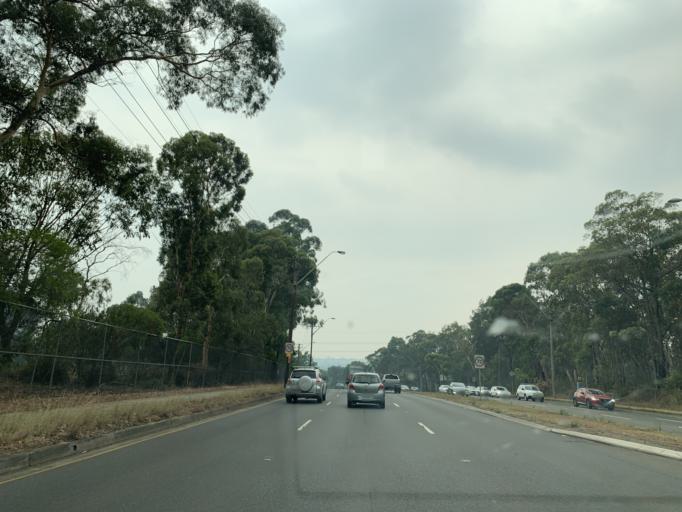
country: AU
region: New South Wales
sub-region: Ryde
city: North Ryde
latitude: -33.7797
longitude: 151.1340
